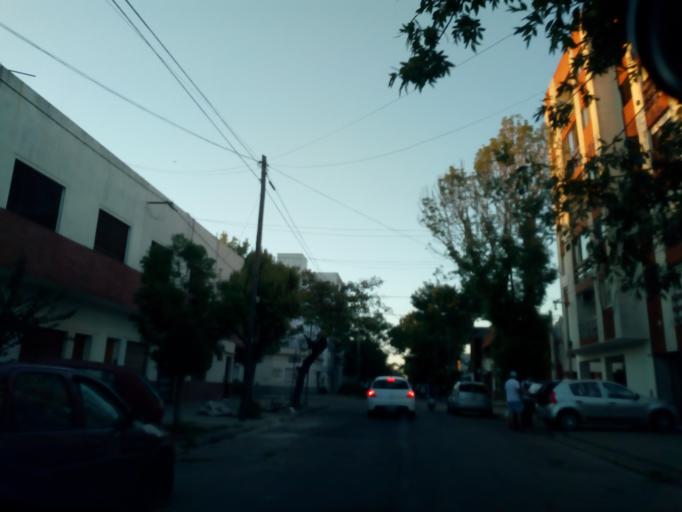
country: AR
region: Buenos Aires
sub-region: Partido de La Plata
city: La Plata
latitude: -34.9232
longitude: -57.9705
